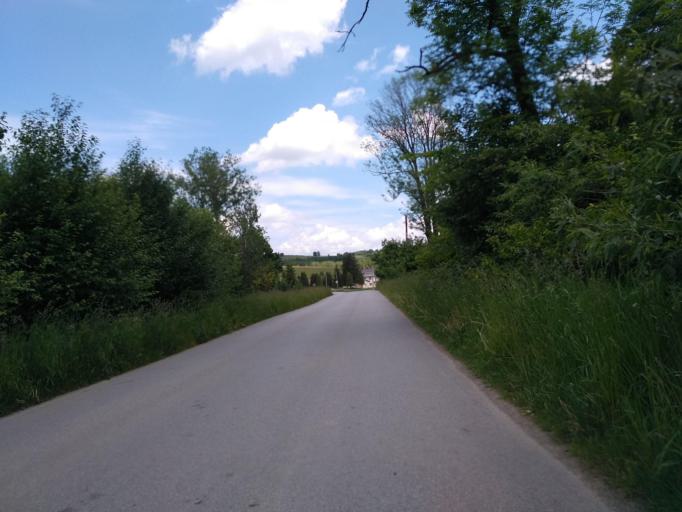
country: PL
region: Subcarpathian Voivodeship
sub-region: Powiat krosnienski
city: Chorkowka
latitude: 49.6066
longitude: 21.6230
